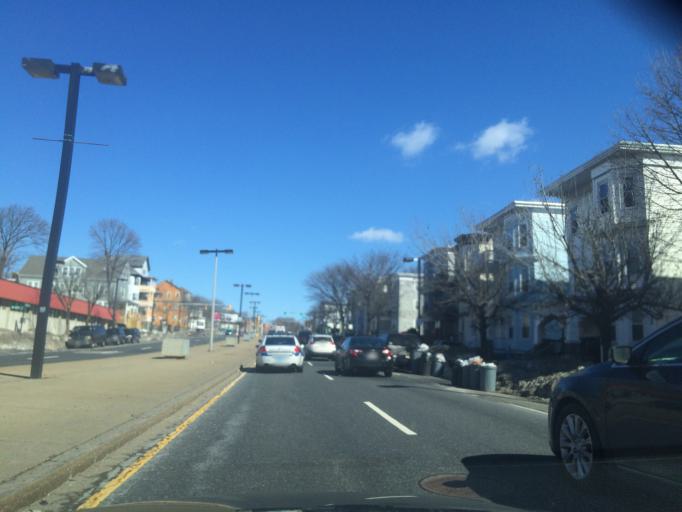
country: US
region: Massachusetts
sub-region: Norfolk County
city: Milton
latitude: 42.2748
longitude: -71.0935
